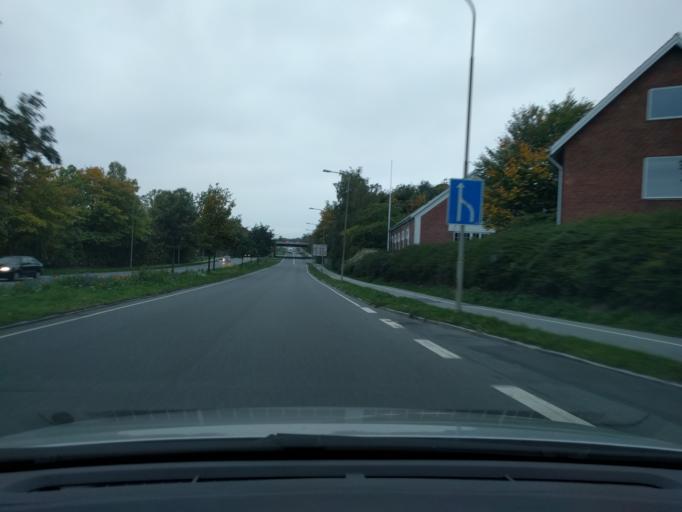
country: DK
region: South Denmark
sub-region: Svendborg Kommune
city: Svendborg
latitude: 55.0606
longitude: 10.5927
